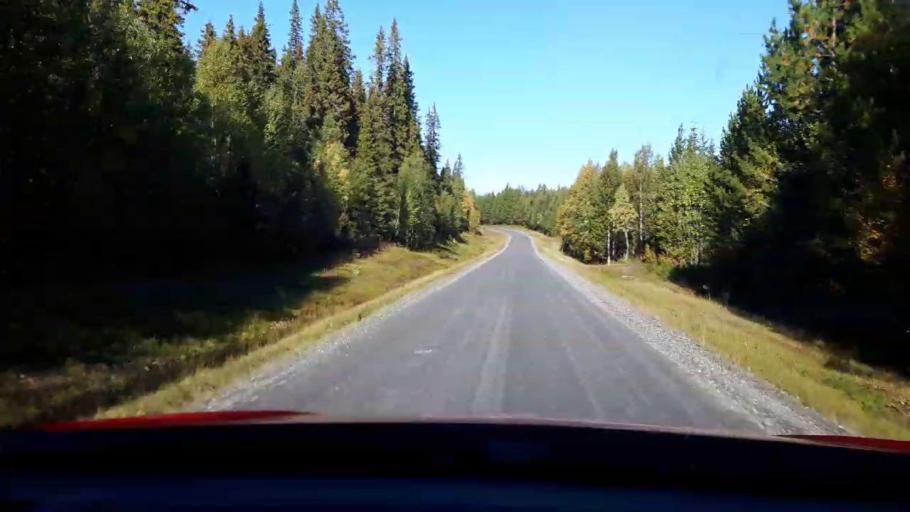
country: NO
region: Nord-Trondelag
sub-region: Lierne
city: Sandvika
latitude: 64.5317
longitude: 14.0380
